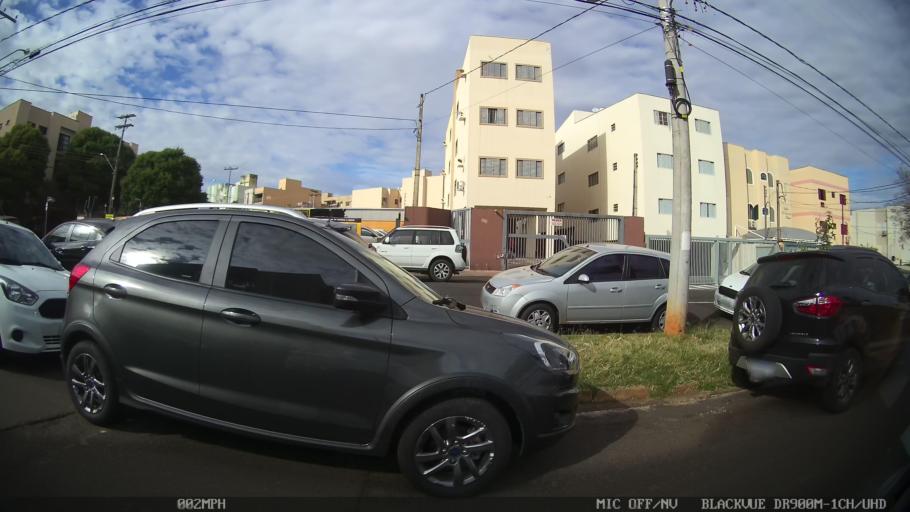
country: BR
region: Sao Paulo
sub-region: Sao Jose Do Rio Preto
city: Sao Jose do Rio Preto
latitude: -20.8279
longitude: -49.4016
